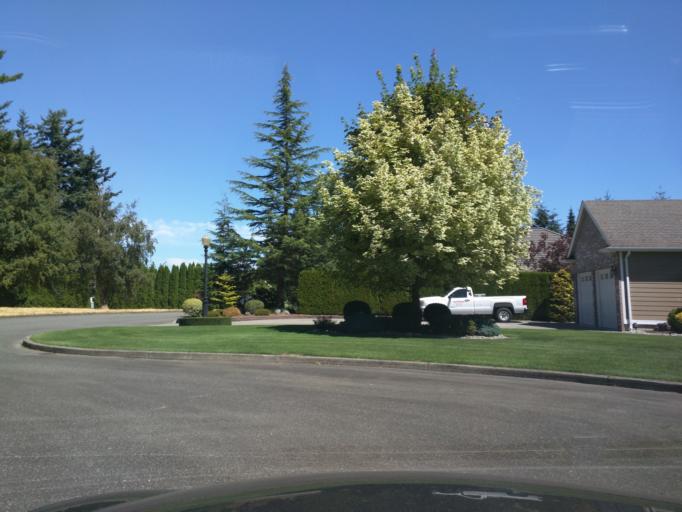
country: US
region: Washington
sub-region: Whatcom County
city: Lynden
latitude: 48.8898
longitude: -122.4479
